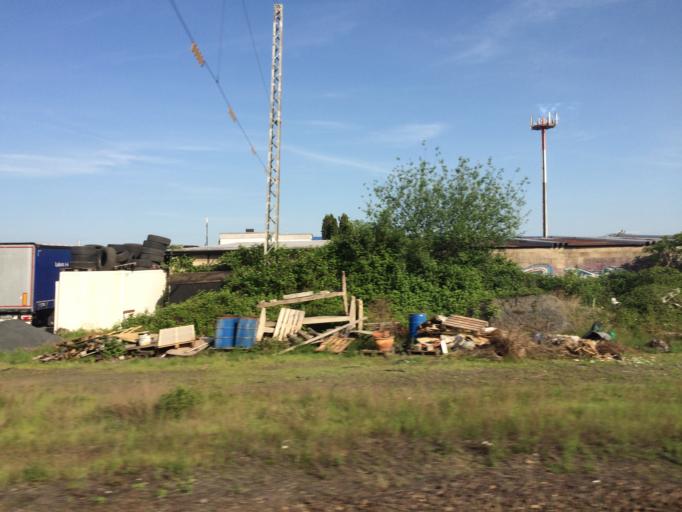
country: DE
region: North Rhine-Westphalia
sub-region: Regierungsbezirk Koln
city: Troisdorf
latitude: 50.7773
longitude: 7.1480
